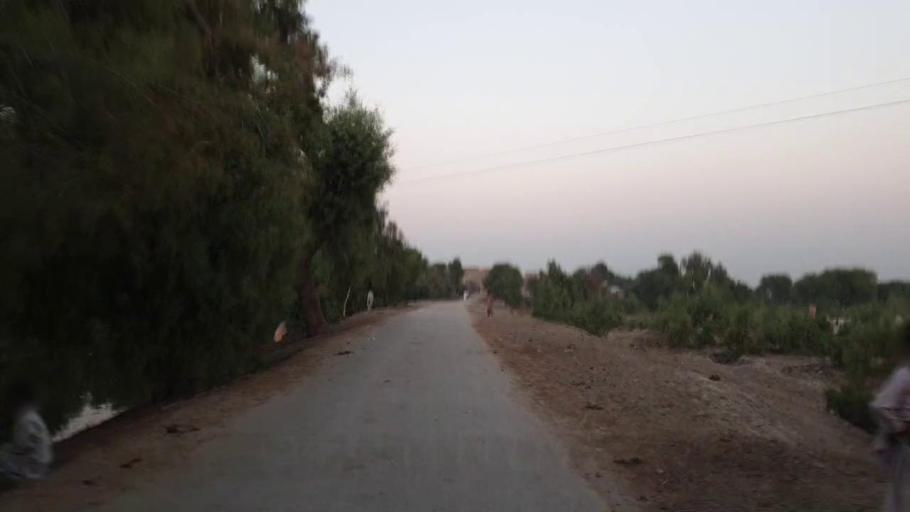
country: PK
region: Sindh
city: Bhan
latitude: 26.4692
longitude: 67.7635
